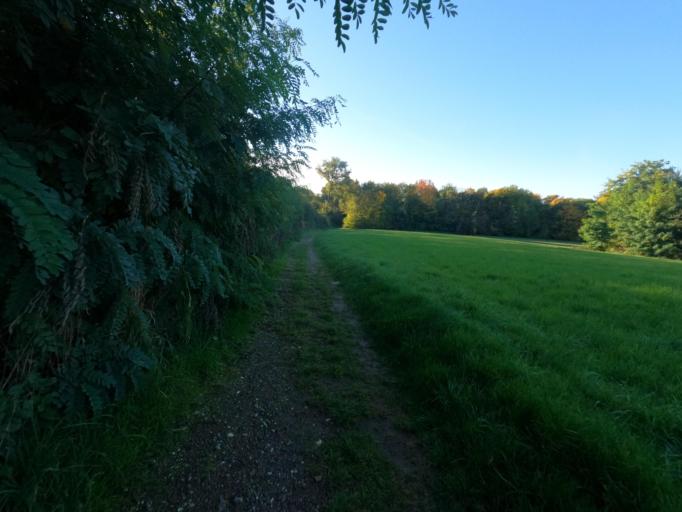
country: DE
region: North Rhine-Westphalia
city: Erkelenz
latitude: 51.0602
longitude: 6.3186
